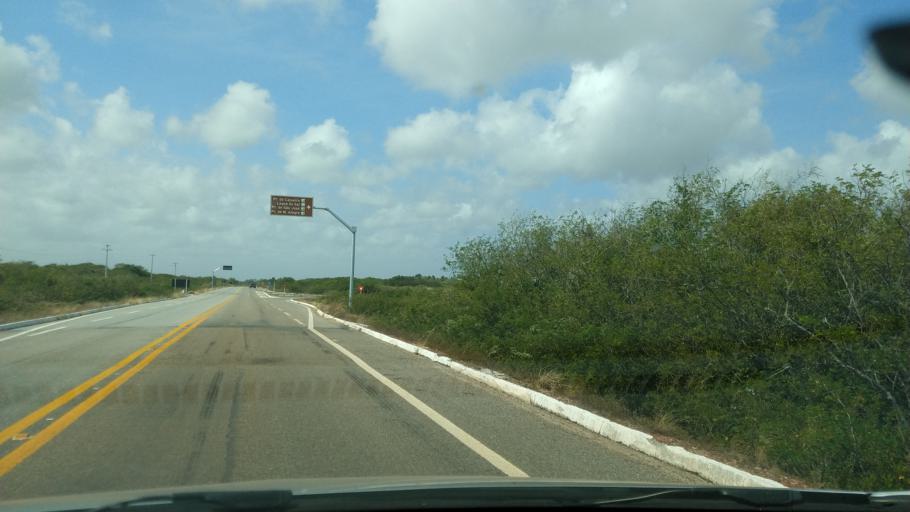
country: BR
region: Rio Grande do Norte
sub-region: Touros
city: Touros
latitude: -5.1714
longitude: -35.5067
